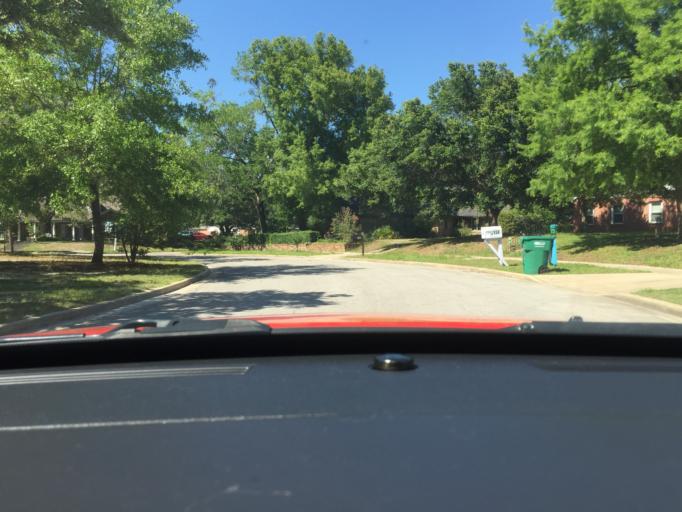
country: US
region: Mississippi
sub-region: Harrison County
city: D'Iberville
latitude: 30.3933
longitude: -88.9866
